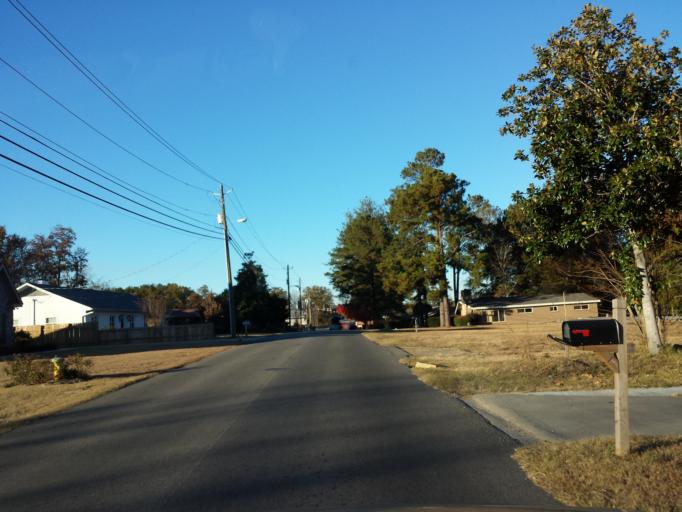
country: US
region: Mississippi
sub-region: Lamar County
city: West Hattiesburg
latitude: 31.3228
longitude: -89.3401
